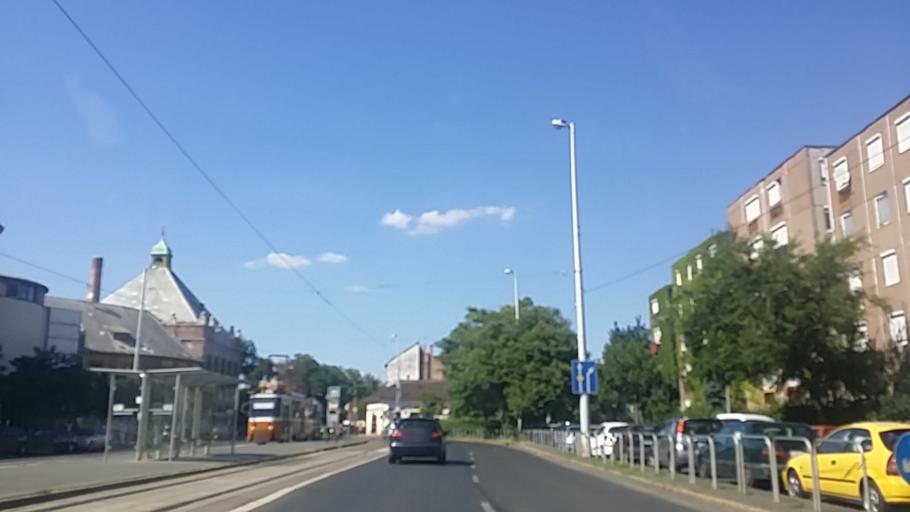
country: HU
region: Budapest
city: Budapest IV. keruelet
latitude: 47.5628
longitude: 19.0908
